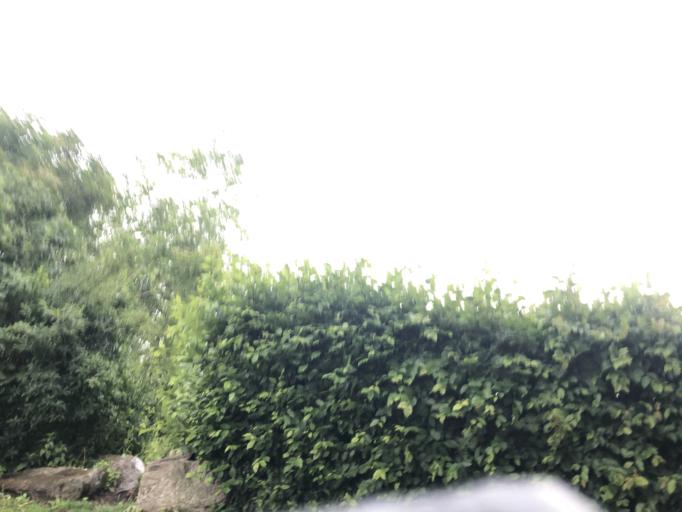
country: DK
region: Capital Region
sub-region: Gladsaxe Municipality
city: Buddinge
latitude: 55.7496
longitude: 12.4891
